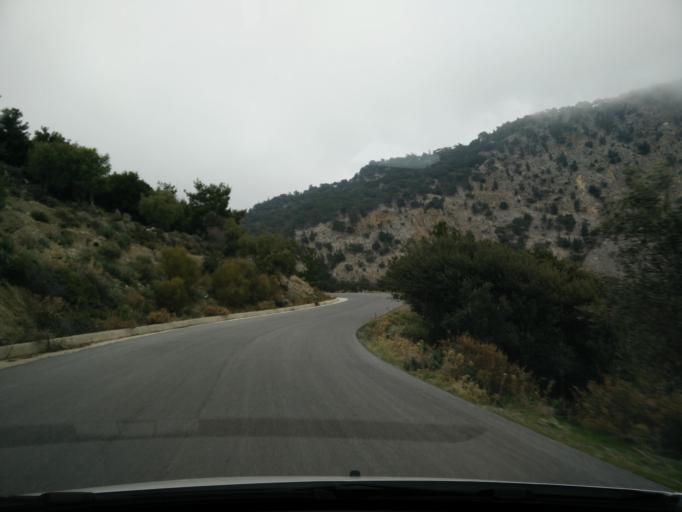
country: GR
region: Crete
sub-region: Nomos Lasithiou
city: Kritsa
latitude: 35.0381
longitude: 25.4877
